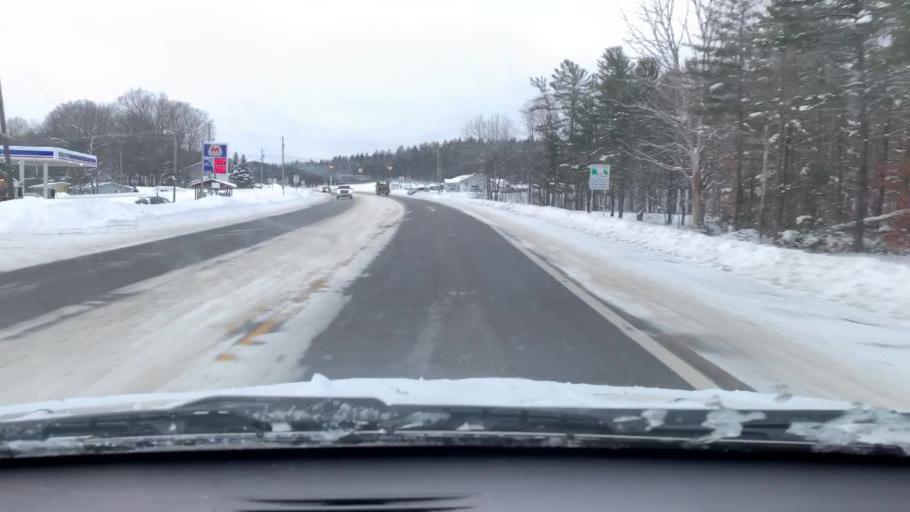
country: US
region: Michigan
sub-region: Kalkaska County
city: Kalkaska
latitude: 44.6423
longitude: -85.2855
